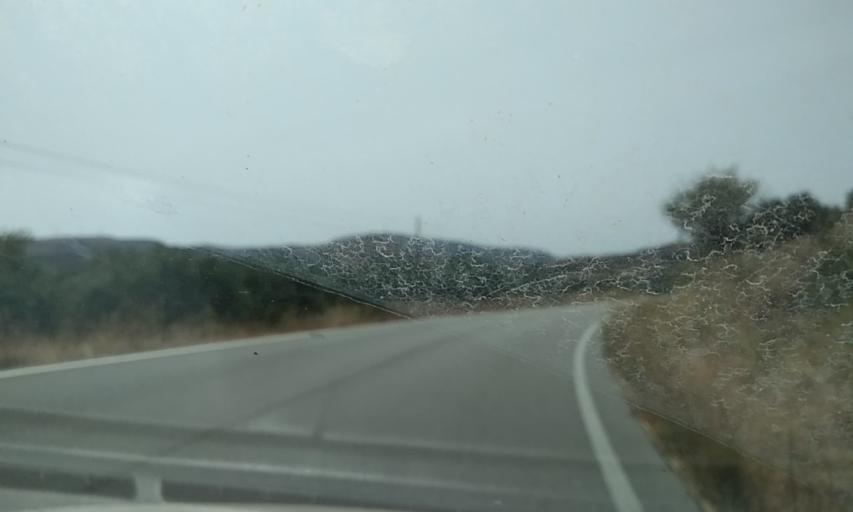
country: GR
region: Crete
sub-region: Nomos Lasithiou
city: Siteia
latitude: 35.1178
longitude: 26.0623
